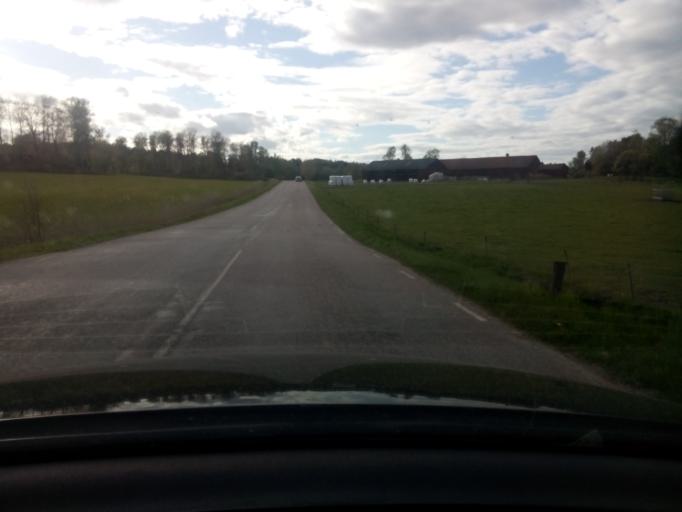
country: SE
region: Soedermanland
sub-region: Nykopings Kommun
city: Stigtomta
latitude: 58.9522
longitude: 16.8657
